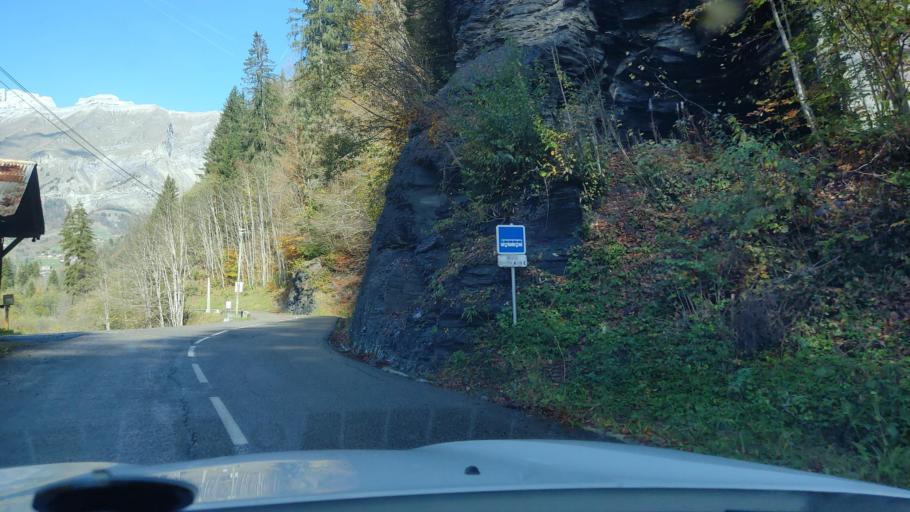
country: FR
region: Rhone-Alpes
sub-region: Departement de la Haute-Savoie
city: Praz-sur-Arly
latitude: 45.8418
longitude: 6.5065
